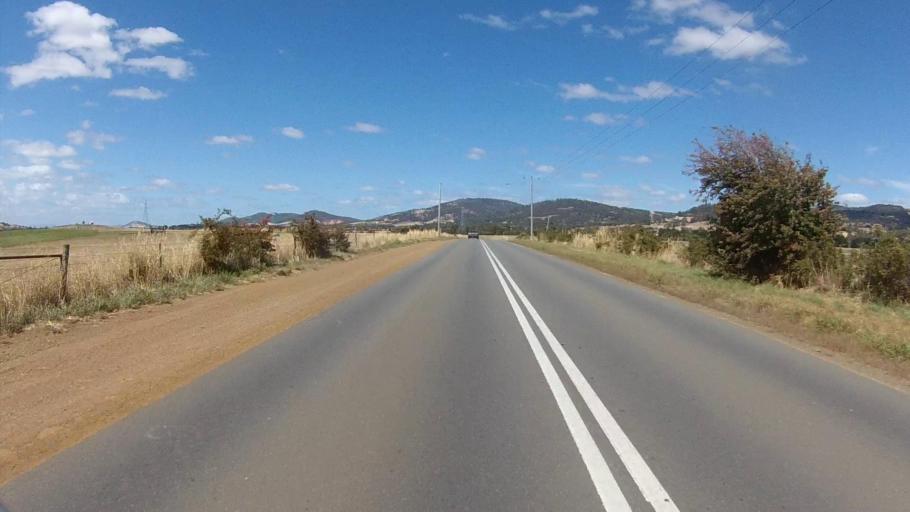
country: AU
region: Tasmania
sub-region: Clarence
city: Cambridge
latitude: -42.7594
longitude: 147.4162
